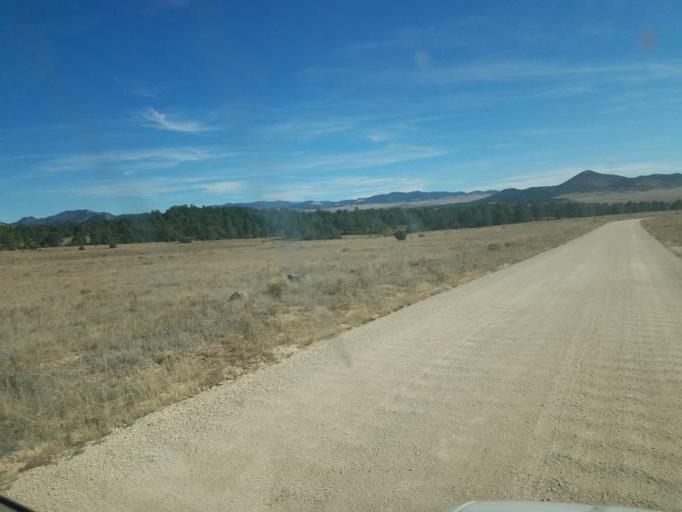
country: US
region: Colorado
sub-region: Custer County
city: Westcliffe
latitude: 38.2322
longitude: -105.4575
